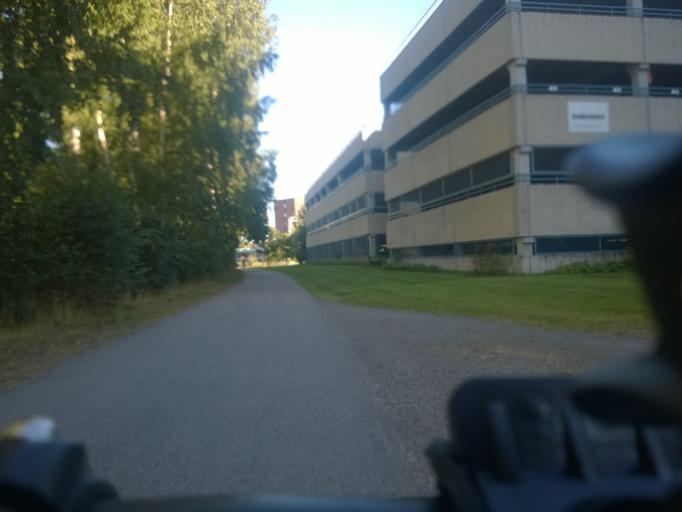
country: FI
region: Uusimaa
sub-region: Helsinki
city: Teekkarikylae
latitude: 60.2227
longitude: 24.8731
